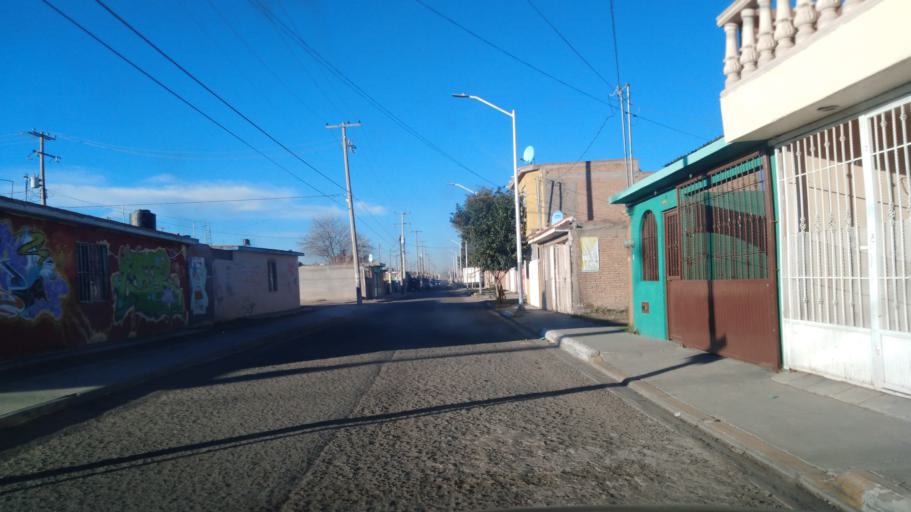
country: MX
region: Durango
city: Victoria de Durango
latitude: 24.0578
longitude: -104.6001
